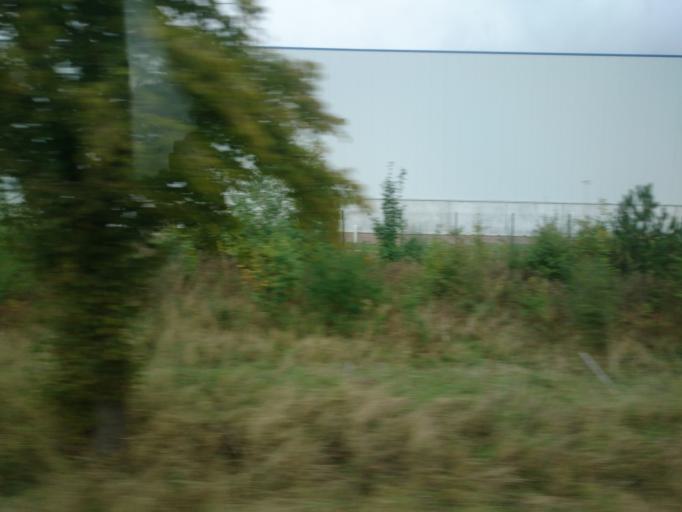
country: DE
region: Saxony-Anhalt
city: Ermlitz
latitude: 51.4090
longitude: 12.1619
